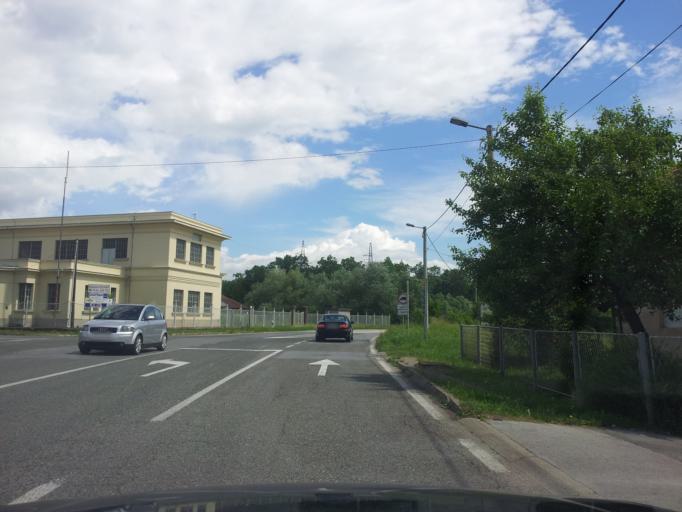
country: HR
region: Karlovacka
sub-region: Grad Karlovac
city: Karlovac
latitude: 45.5194
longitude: 15.5456
